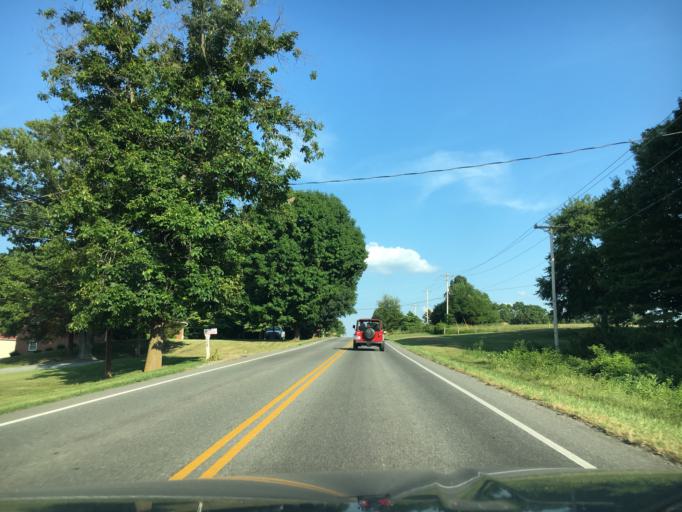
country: US
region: Virginia
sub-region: Franklin County
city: Henry Fork
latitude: 37.0134
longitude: -79.7992
